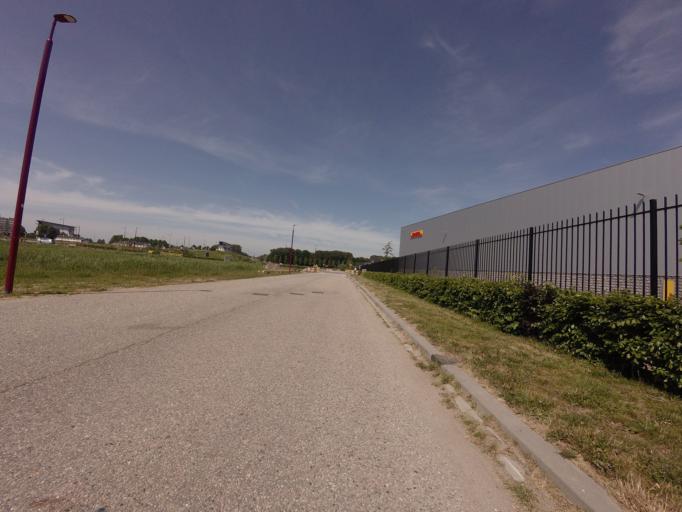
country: NL
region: Utrecht
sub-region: Gemeente Vianen
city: Vianen
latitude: 52.0149
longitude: 5.1168
